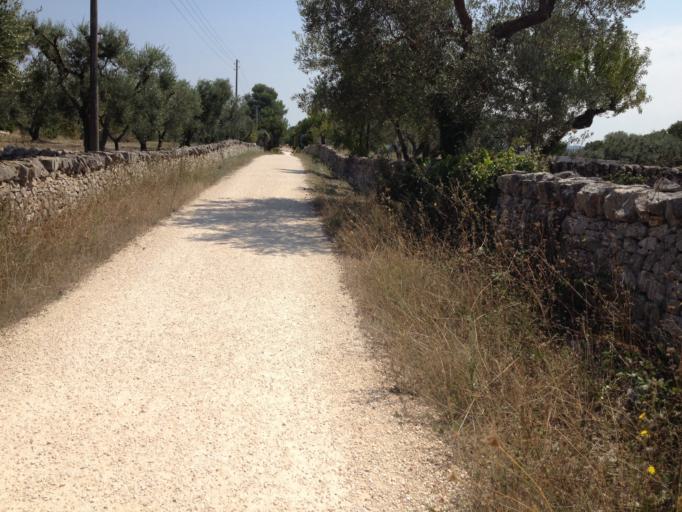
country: IT
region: Apulia
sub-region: Provincia di Brindisi
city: Cisternino
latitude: 40.7152
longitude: 17.4067
